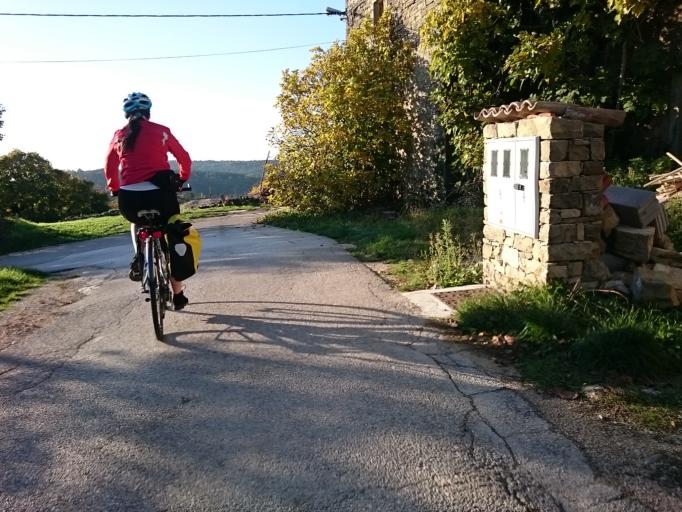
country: HR
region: Istarska
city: Buje
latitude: 45.3842
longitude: 13.7139
